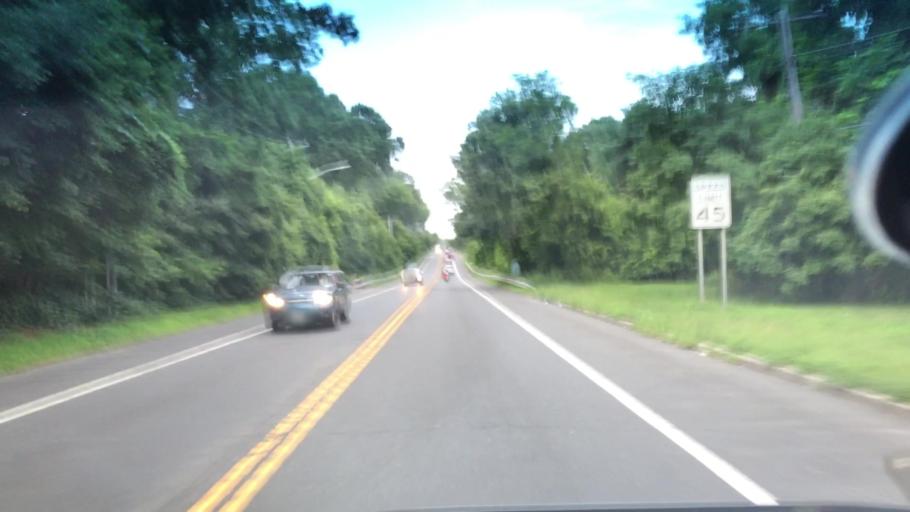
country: US
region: New York
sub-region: Suffolk County
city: Wading River
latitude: 40.9437
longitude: -72.8588
